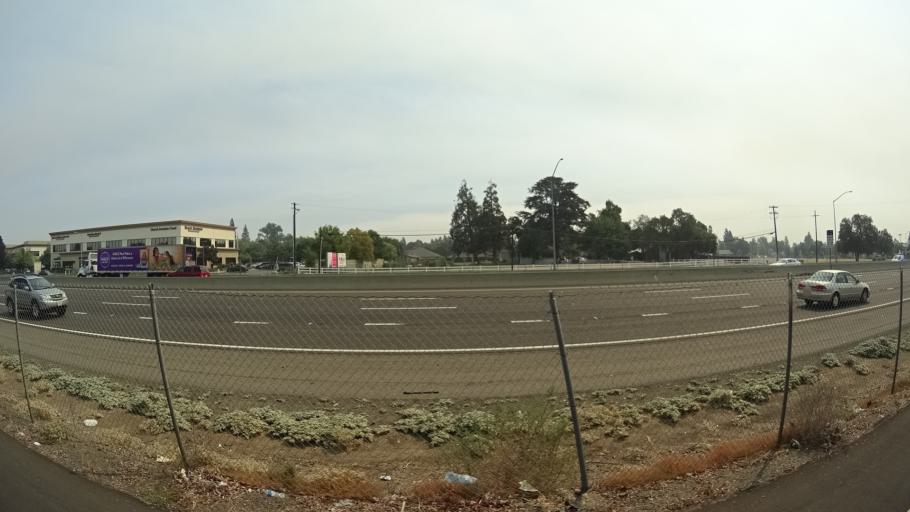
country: US
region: California
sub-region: Sacramento County
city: Elk Grove
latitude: 38.4147
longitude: -121.3918
